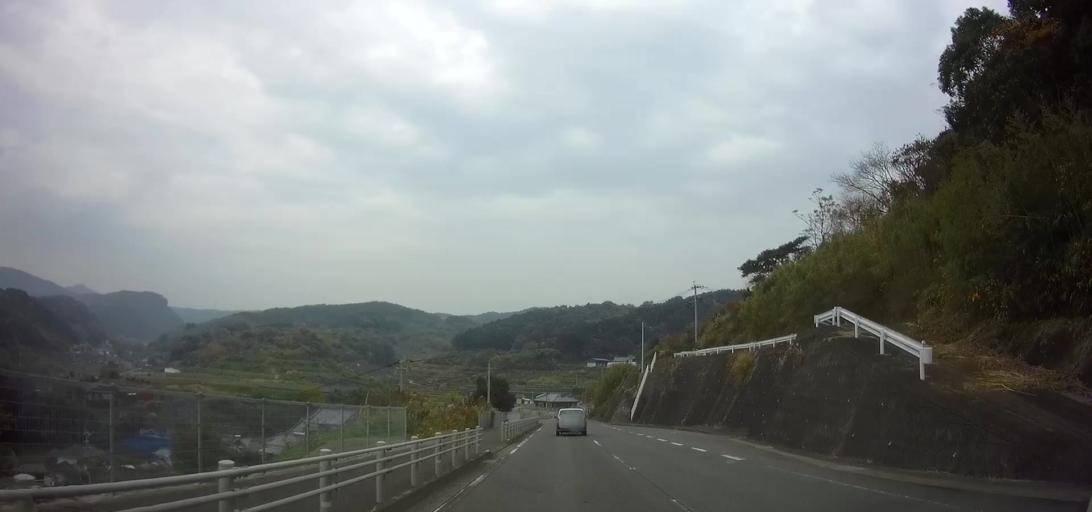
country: JP
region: Nagasaki
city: Shimabara
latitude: 32.7056
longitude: 130.1864
